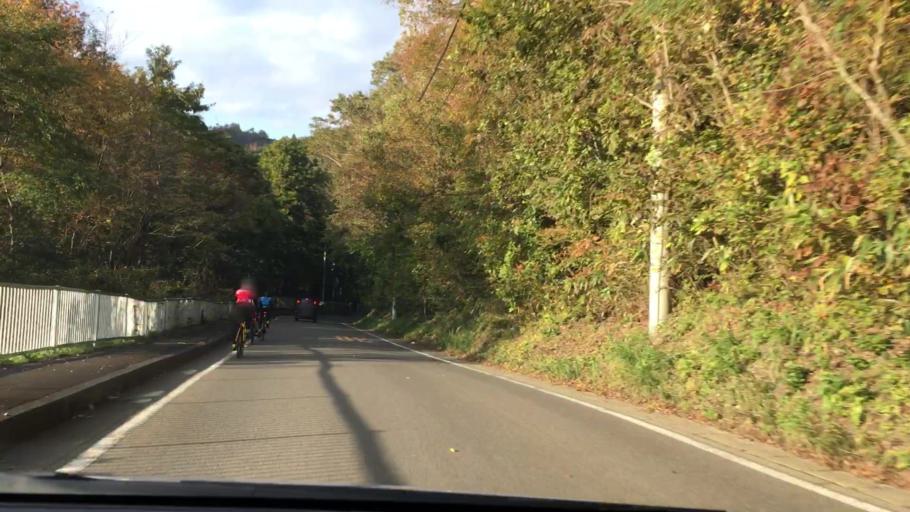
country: JP
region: Yamanashi
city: Uenohara
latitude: 35.5473
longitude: 139.1323
